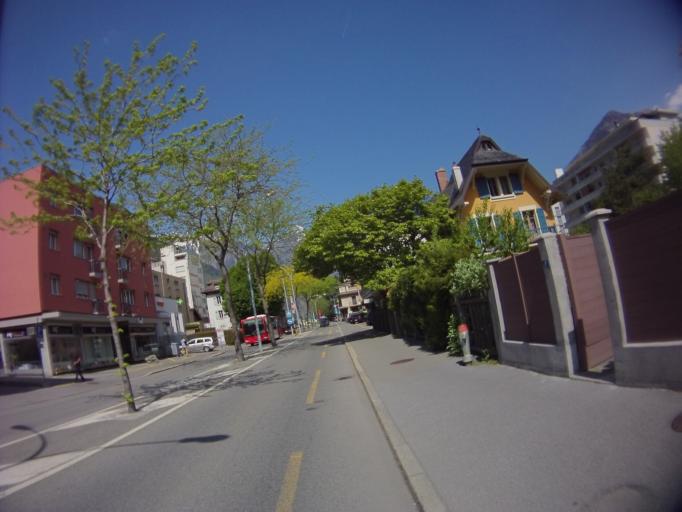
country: CH
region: Valais
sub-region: Martigny District
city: Martigny-Ville
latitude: 46.1036
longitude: 7.0779
